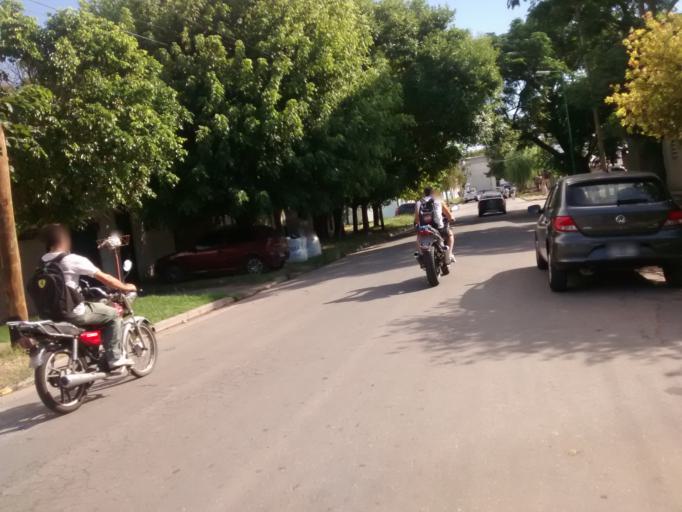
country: AR
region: Buenos Aires
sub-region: Partido de La Plata
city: La Plata
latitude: -34.9539
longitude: -57.9488
